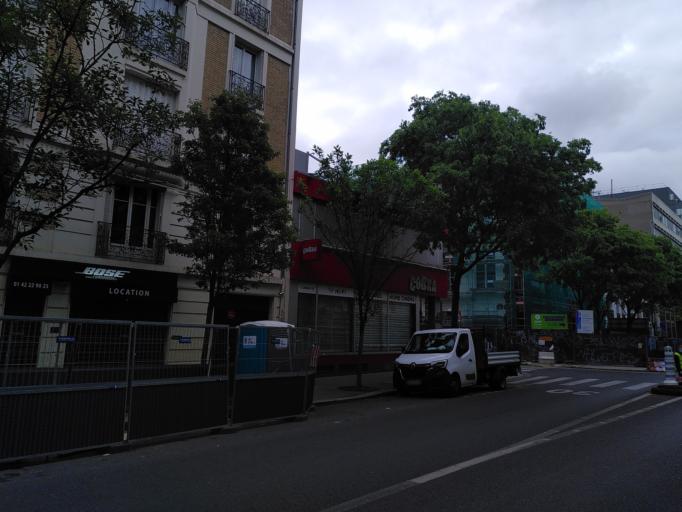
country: FR
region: Ile-de-France
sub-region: Paris
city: Paris
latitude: 48.8635
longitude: 2.3760
